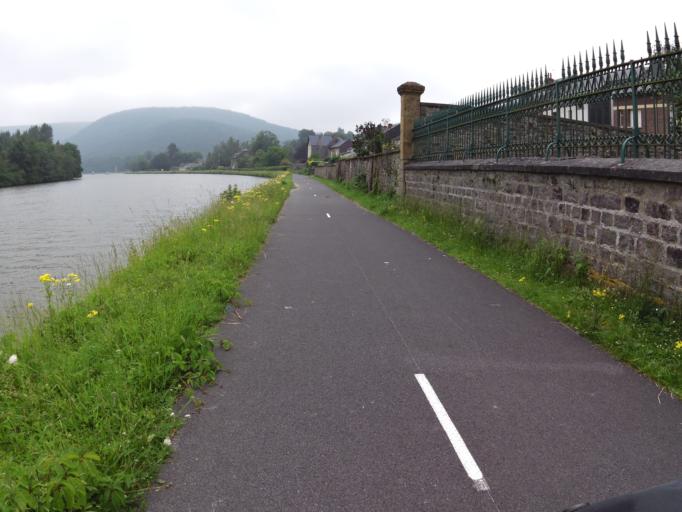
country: FR
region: Champagne-Ardenne
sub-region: Departement des Ardennes
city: Haybes
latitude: 50.0103
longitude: 4.7133
